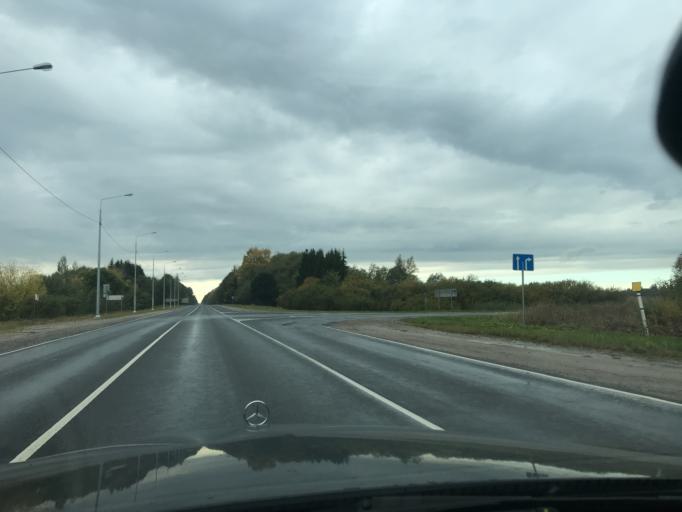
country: RU
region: Pskov
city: Izborsk
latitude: 57.7044
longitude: 27.8472
